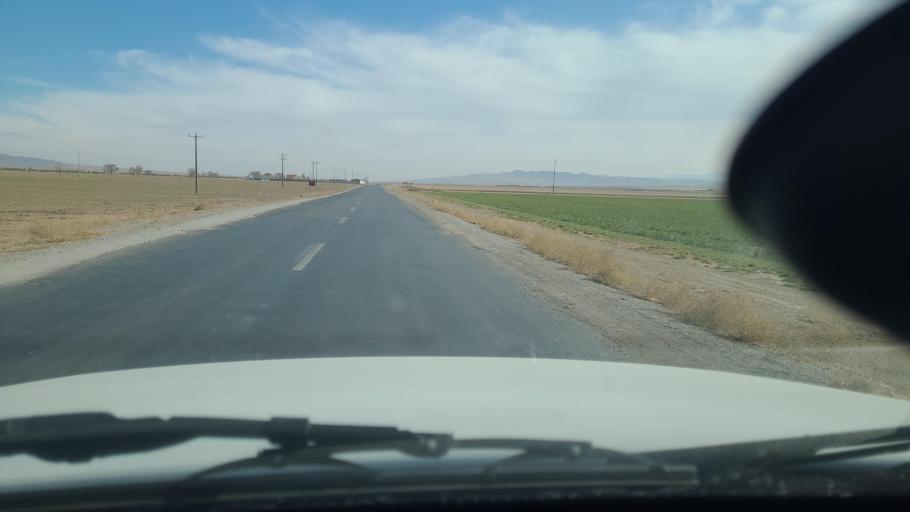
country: IR
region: Razavi Khorasan
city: Dowlatabad
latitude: 35.6002
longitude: 59.4618
